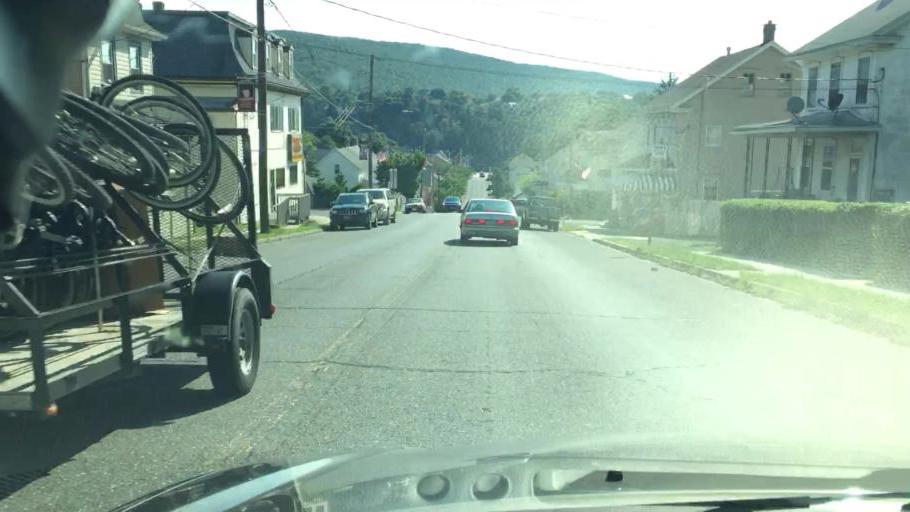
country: US
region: Pennsylvania
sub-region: Carbon County
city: Jim Thorpe
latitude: 40.8739
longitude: -75.7338
